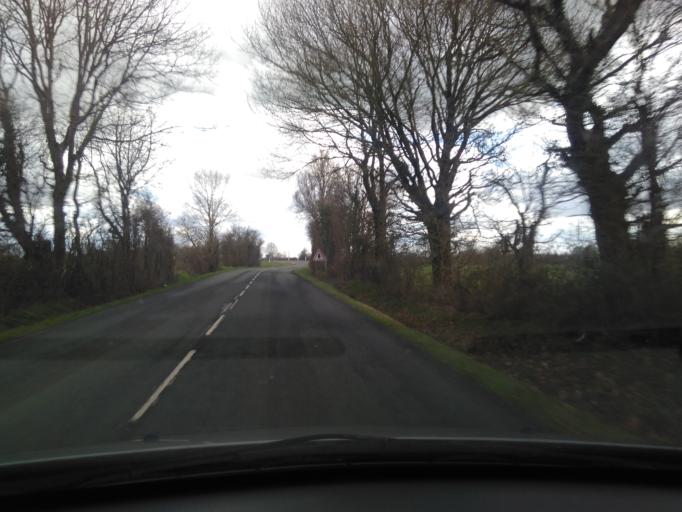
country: FR
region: Pays de la Loire
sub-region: Departement de la Vendee
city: Les Essarts
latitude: 46.7515
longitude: -1.2137
